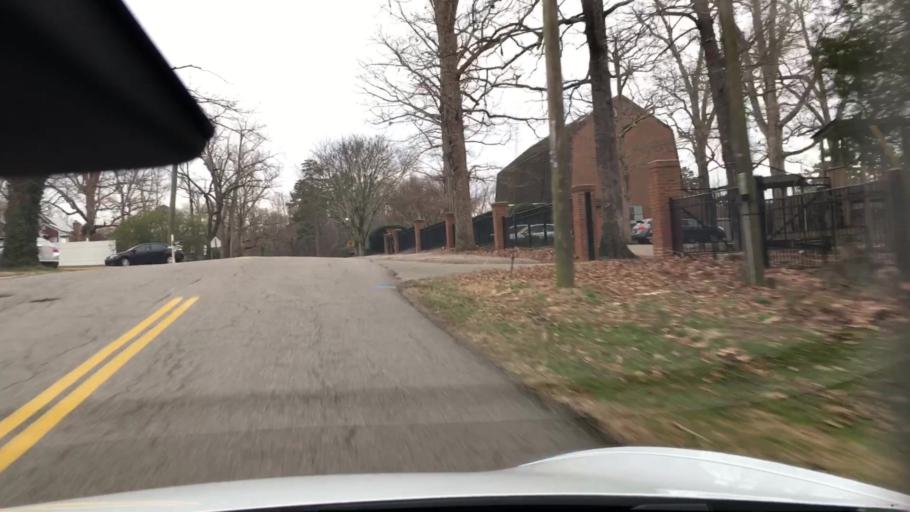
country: US
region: Virginia
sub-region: Chesterfield County
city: Bon Air
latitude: 37.5261
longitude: -77.5598
